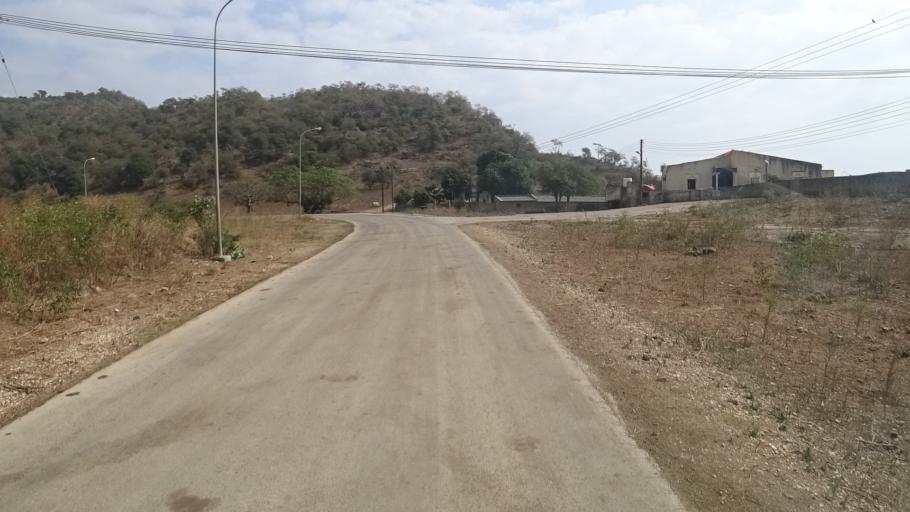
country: YE
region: Al Mahrah
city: Hawf
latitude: 16.7197
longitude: 53.2681
